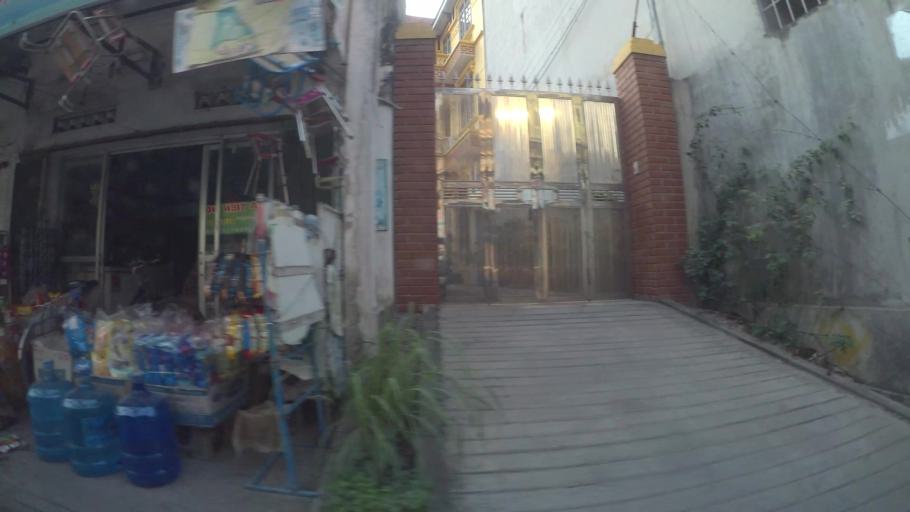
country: VN
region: Ha Noi
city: Van Dien
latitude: 20.9333
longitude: 105.8362
